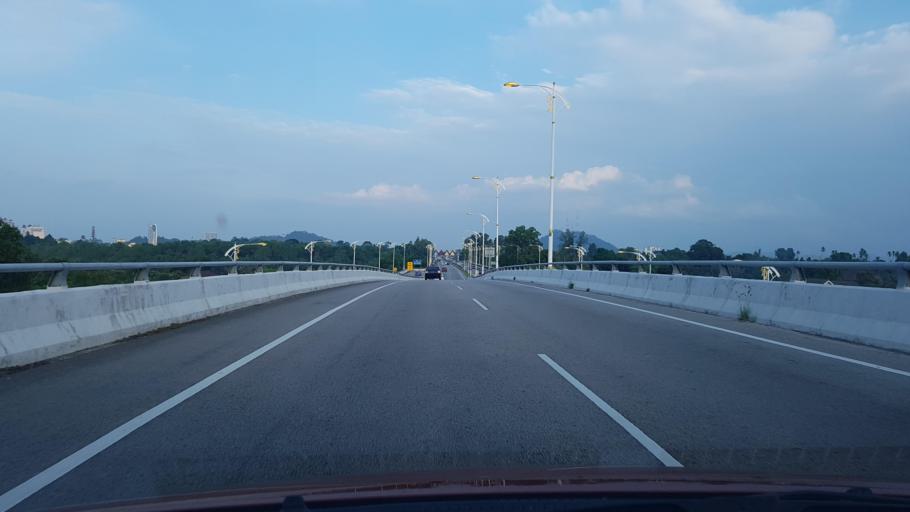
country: MY
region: Terengganu
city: Kuala Terengganu
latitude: 5.3371
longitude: 103.1141
